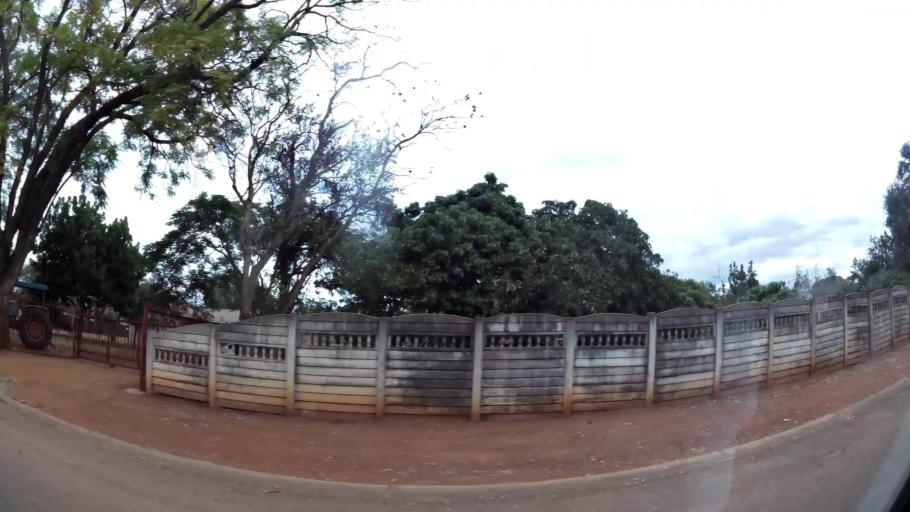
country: ZA
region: Limpopo
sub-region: Waterberg District Municipality
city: Modimolle
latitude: -24.5205
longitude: 28.7045
